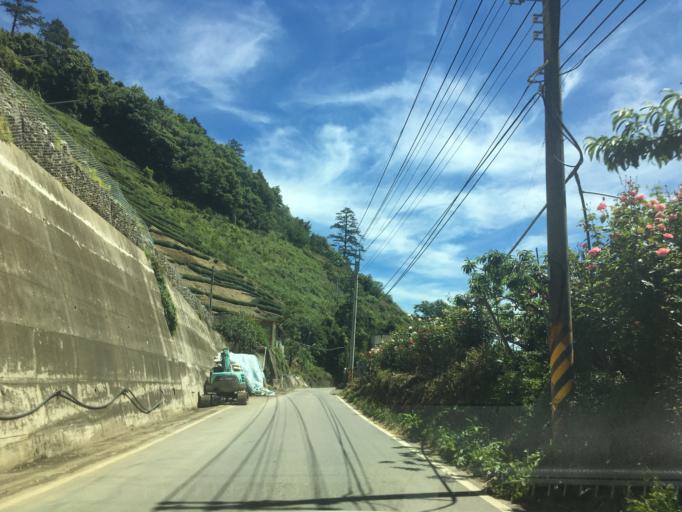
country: TW
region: Taiwan
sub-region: Nantou
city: Puli
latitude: 24.2322
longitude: 121.2534
